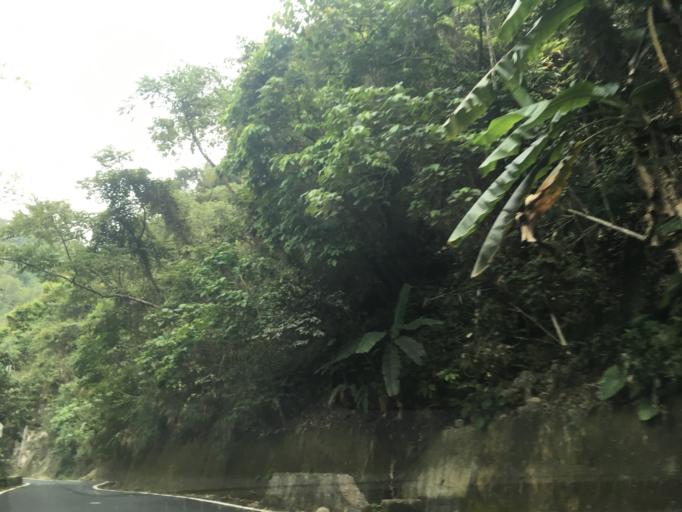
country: TW
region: Taiwan
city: Zhongxing New Village
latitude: 23.9859
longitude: 120.8116
